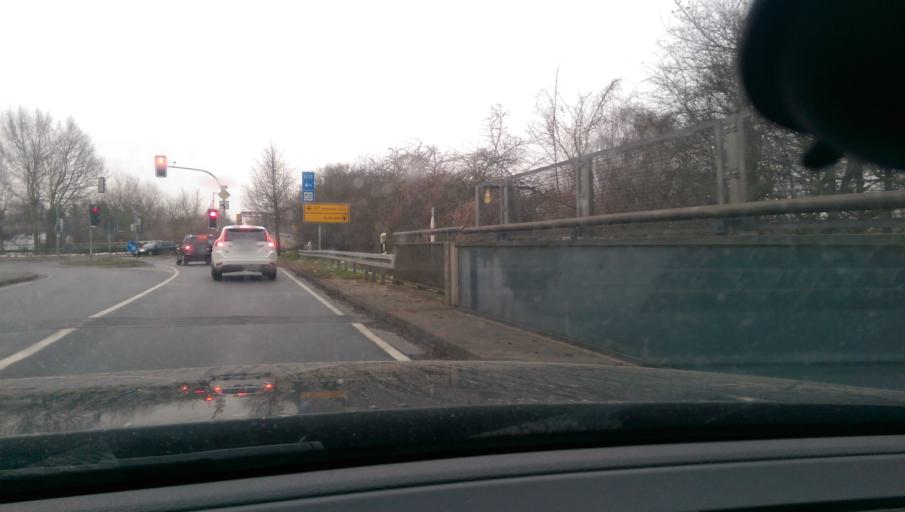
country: DE
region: Lower Saxony
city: Gross Munzel
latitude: 52.4075
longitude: 9.5178
